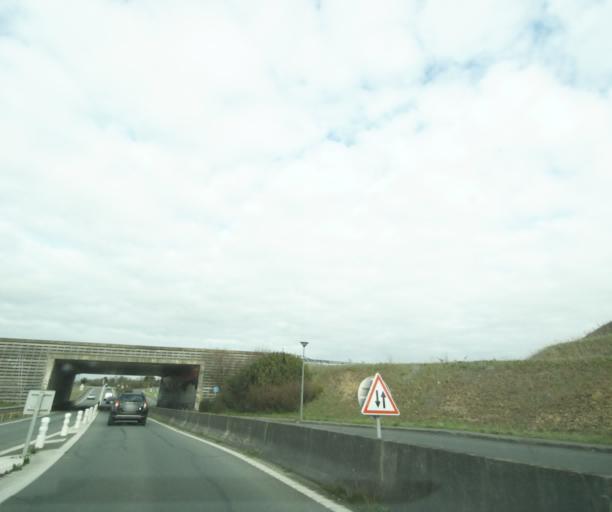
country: FR
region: Poitou-Charentes
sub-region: Departement de la Charente-Maritime
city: Puilboreau
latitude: 46.1759
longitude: -1.1264
